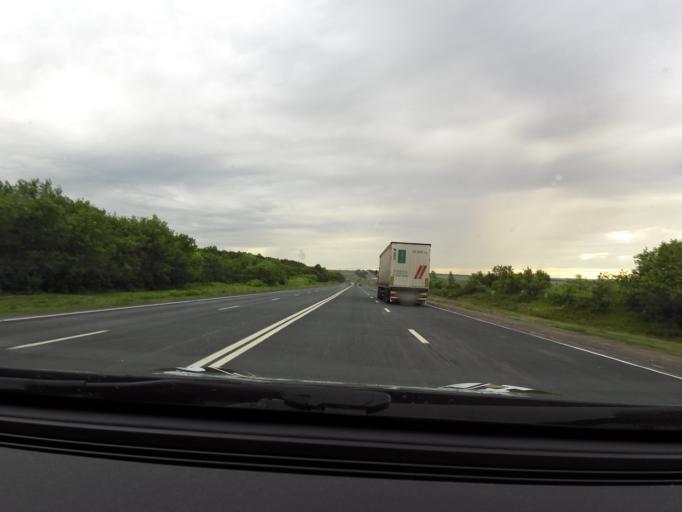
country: RU
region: Chuvashia
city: Yantikovo
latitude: 55.8099
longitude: 47.9889
